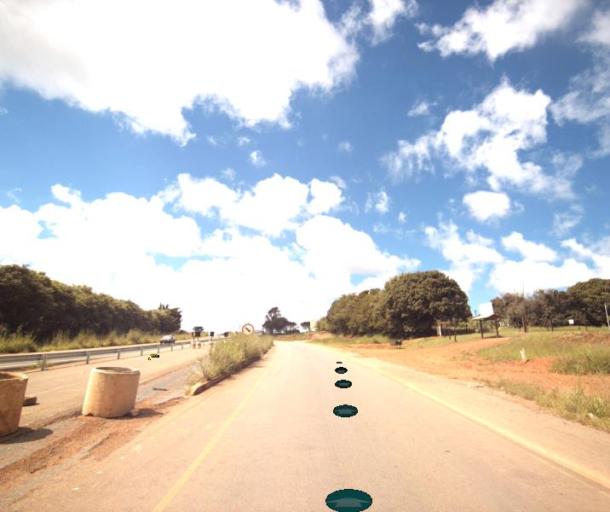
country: BR
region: Goias
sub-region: Anapolis
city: Anapolis
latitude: -16.2450
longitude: -49.0018
